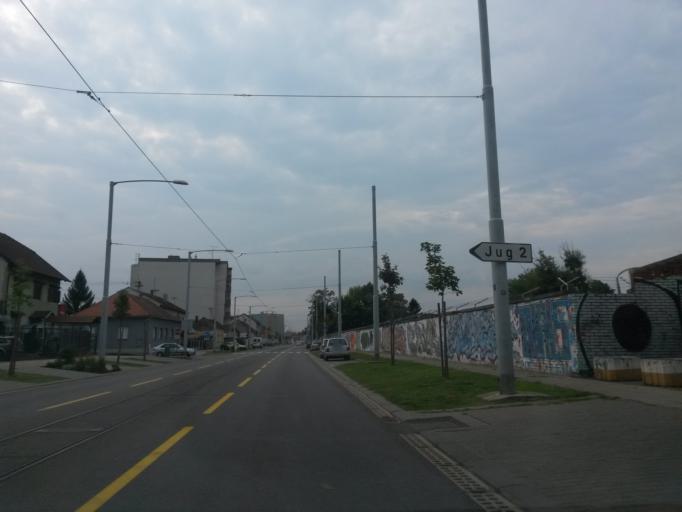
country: HR
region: Osjecko-Baranjska
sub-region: Grad Osijek
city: Osijek
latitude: 45.5485
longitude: 18.7239
